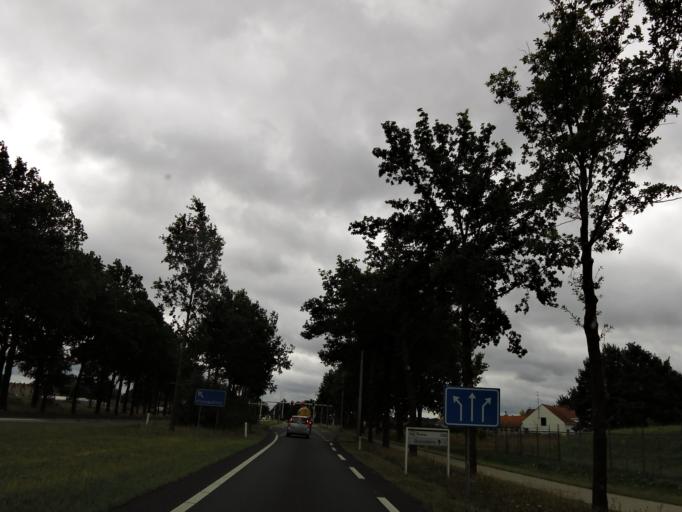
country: NL
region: Limburg
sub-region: Gemeente Sittard-Geleen
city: Limbricht
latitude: 51.0373
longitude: 5.8482
